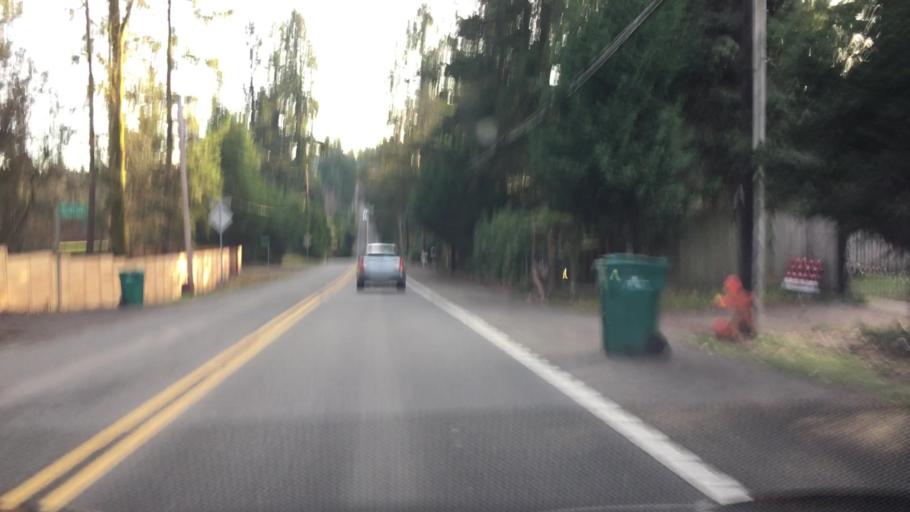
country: US
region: Washington
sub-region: King County
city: Woodinville
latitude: 47.7680
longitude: -122.1317
